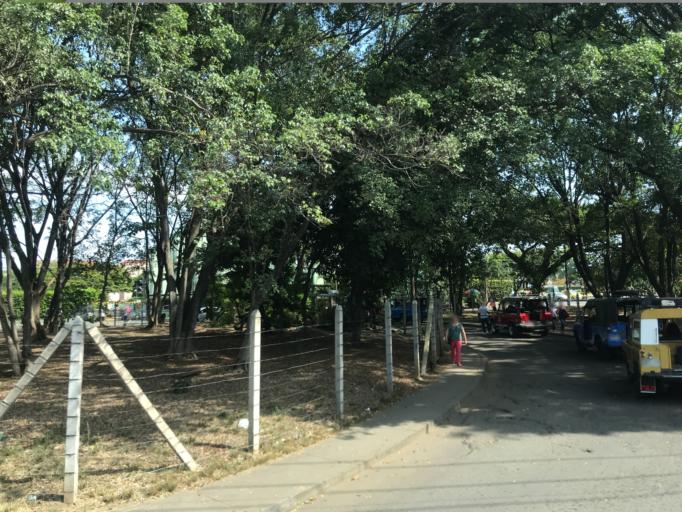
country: CO
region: Valle del Cauca
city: Cali
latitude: 3.4880
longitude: -76.4989
